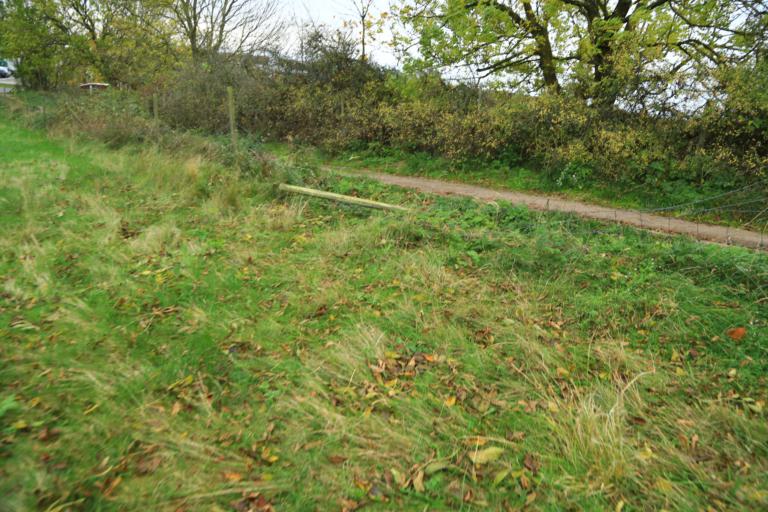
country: SE
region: Halland
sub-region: Varbergs Kommun
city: Varberg
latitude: 57.1275
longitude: 12.2785
